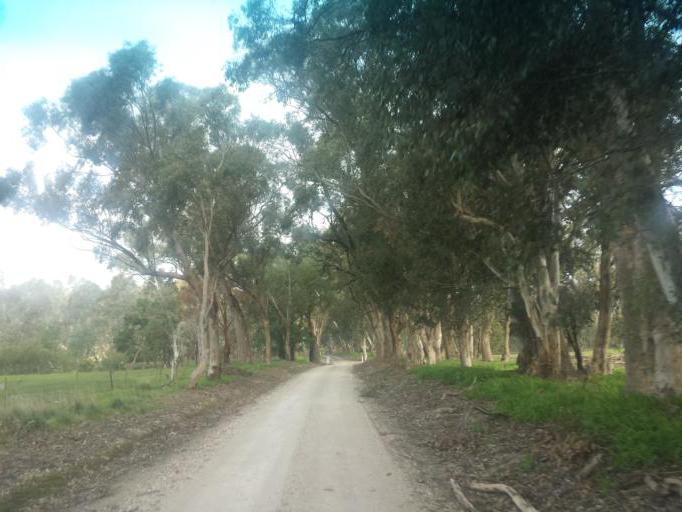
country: AU
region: Victoria
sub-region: Murrindindi
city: Kinglake West
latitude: -37.0374
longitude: 145.2318
